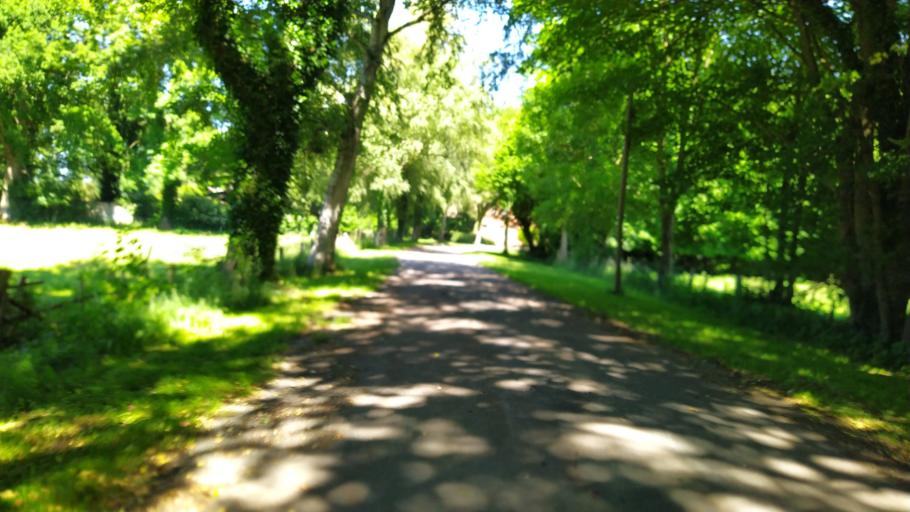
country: DE
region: Lower Saxony
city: Heinbockel
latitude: 53.5373
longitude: 9.3422
